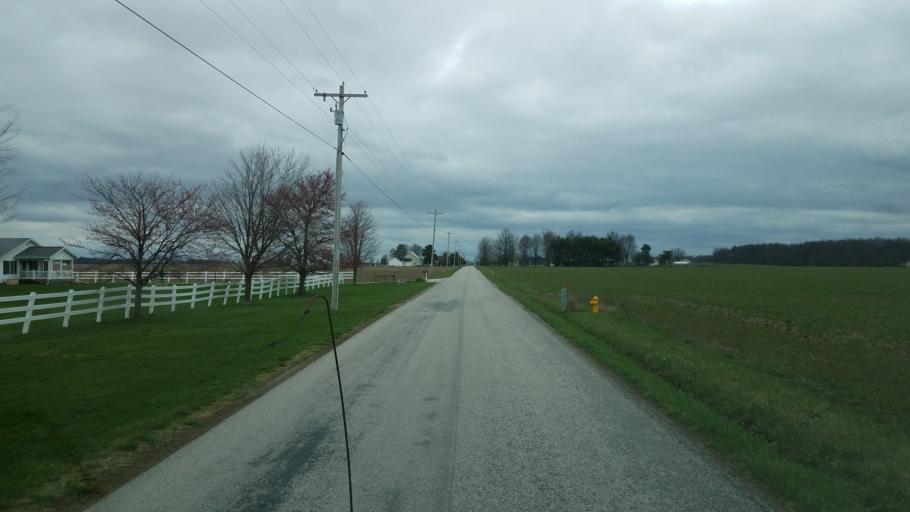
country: US
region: Ohio
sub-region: Delaware County
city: Delaware
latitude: 40.3754
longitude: -83.1196
